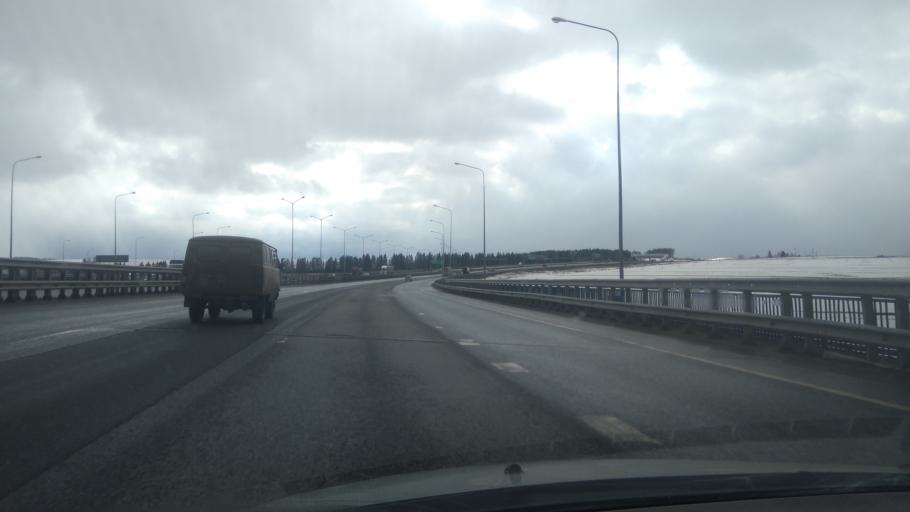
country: RU
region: Perm
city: Lobanovo
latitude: 57.8448
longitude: 56.2929
